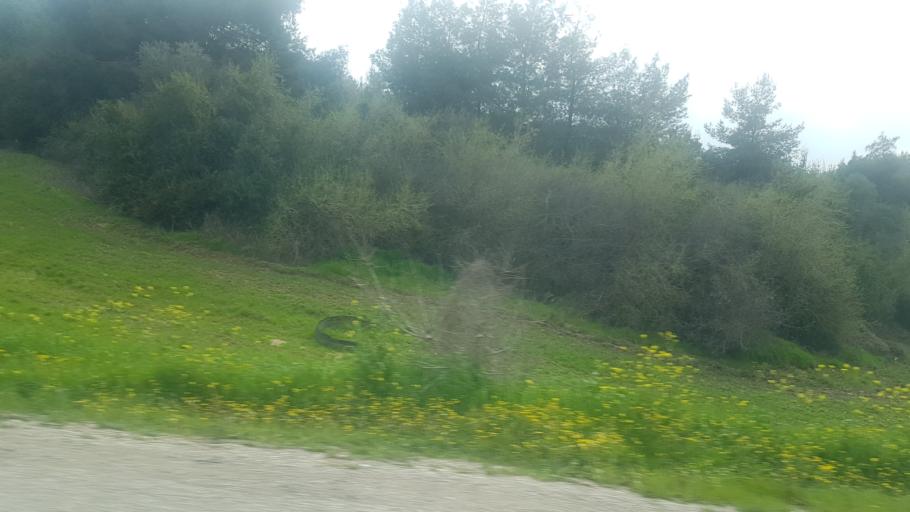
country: TR
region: Mersin
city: Yenice
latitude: 37.0879
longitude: 35.1626
